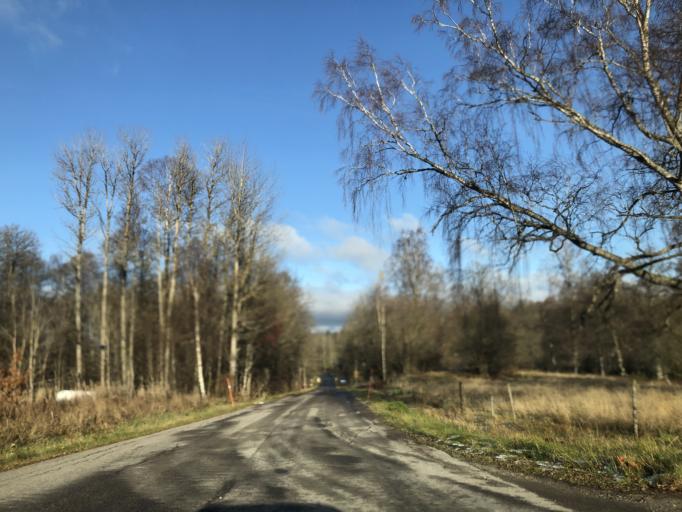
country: SE
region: Vaestra Goetaland
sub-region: Ulricehamns Kommun
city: Ulricehamn
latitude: 57.7302
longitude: 13.4322
